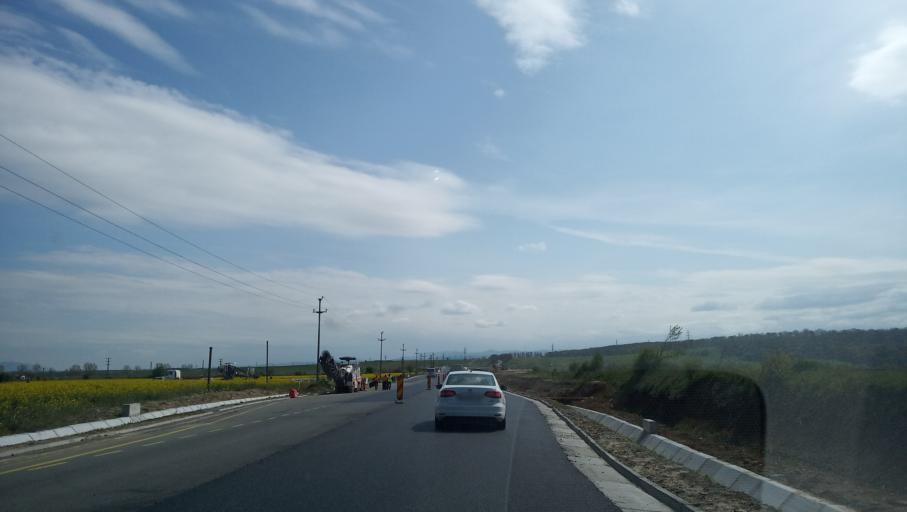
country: RO
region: Hunedoara
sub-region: Comuna Turdas
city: Turdas
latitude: 45.8405
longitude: 23.1345
